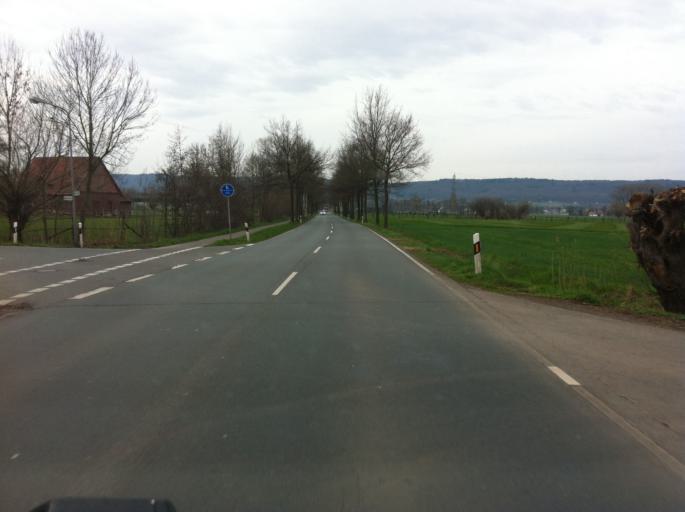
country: DE
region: North Rhine-Westphalia
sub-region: Regierungsbezirk Detmold
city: Minden
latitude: 52.2907
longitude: 8.8633
